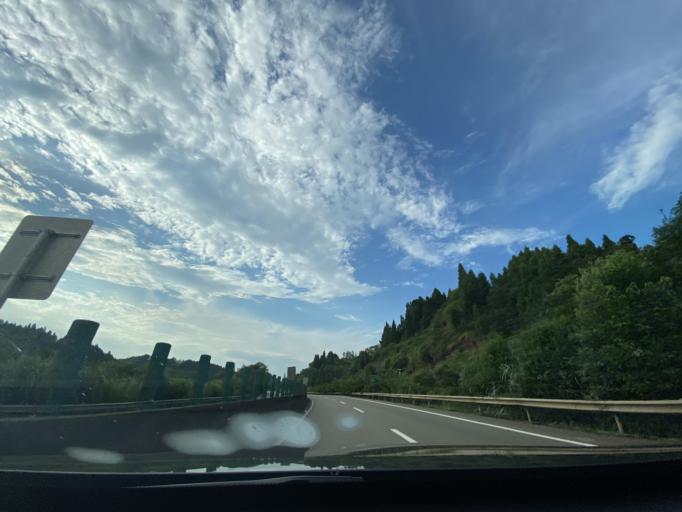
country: CN
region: Sichuan
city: Yanjiang
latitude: 30.2579
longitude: 104.6087
